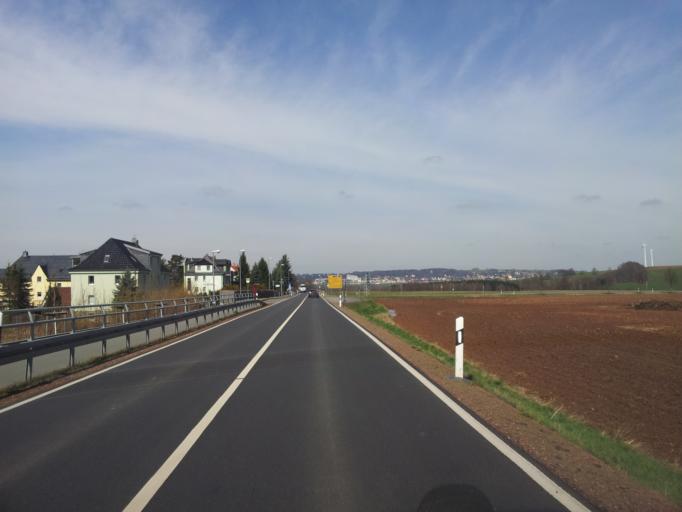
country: DE
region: Saxony
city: Gersdorf
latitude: 50.7589
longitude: 12.7185
